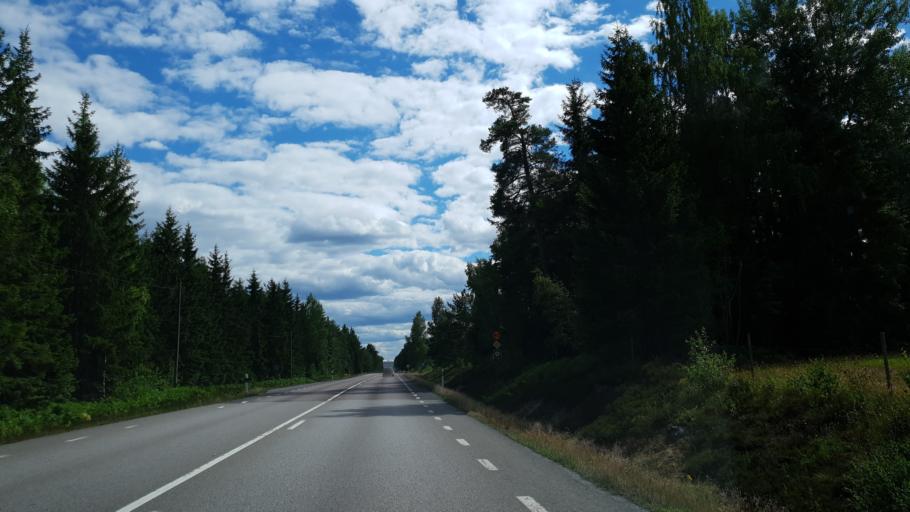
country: SE
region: Kronoberg
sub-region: Uppvidinge Kommun
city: Lenhovda
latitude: 56.8707
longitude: 15.3863
